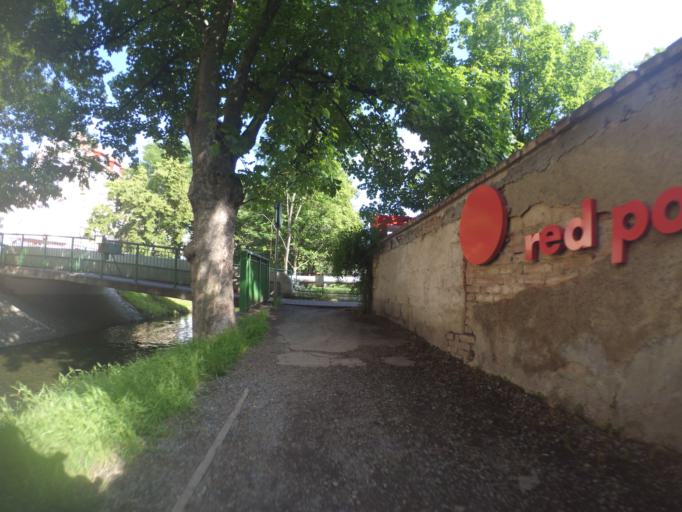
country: CZ
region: Praha
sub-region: Praha 9
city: Prosek
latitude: 50.1083
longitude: 14.4984
